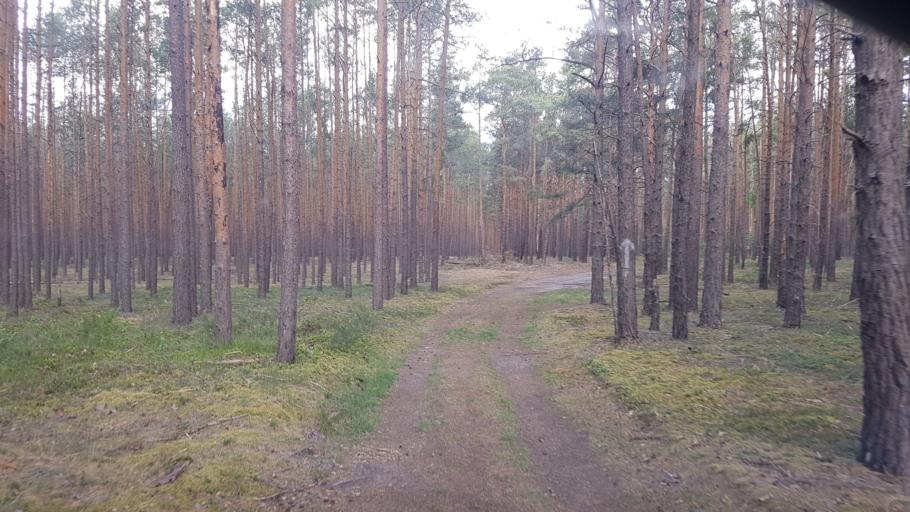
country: DE
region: Brandenburg
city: Finsterwalde
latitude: 51.6449
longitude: 13.6602
